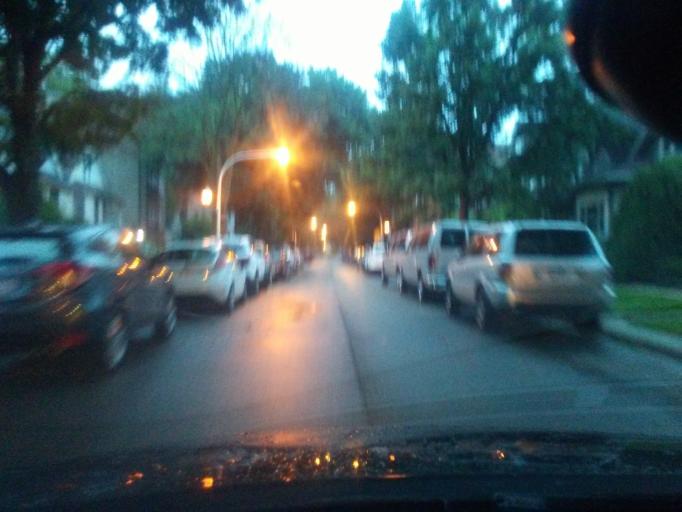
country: US
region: Illinois
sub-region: Cook County
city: Evanston
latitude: 41.9933
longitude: -87.6719
